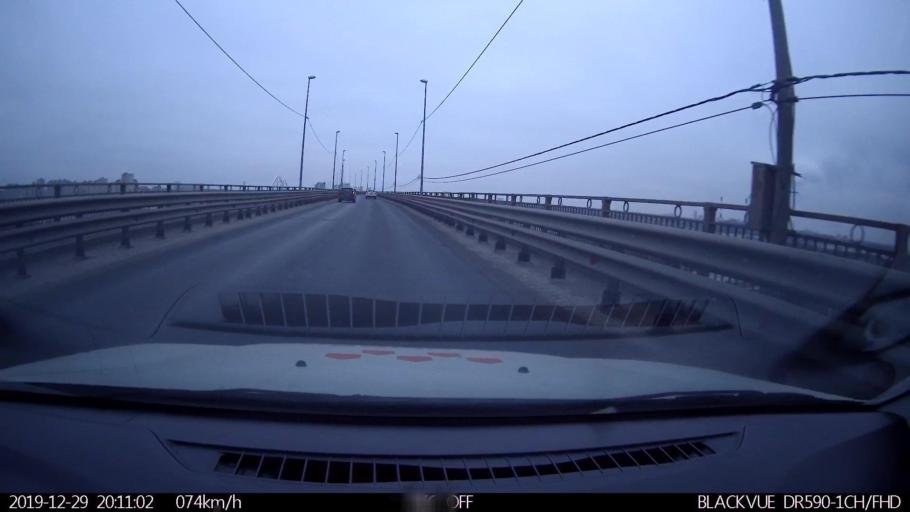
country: RU
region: Nizjnij Novgorod
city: Neklyudovo
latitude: 56.3602
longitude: 43.9299
